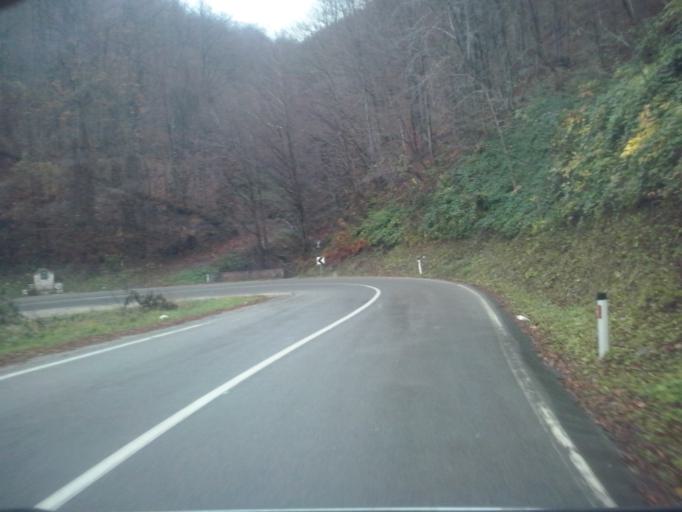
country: RS
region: Central Serbia
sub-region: Moravicki Okrug
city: Ivanjica
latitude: 43.5436
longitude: 20.2667
